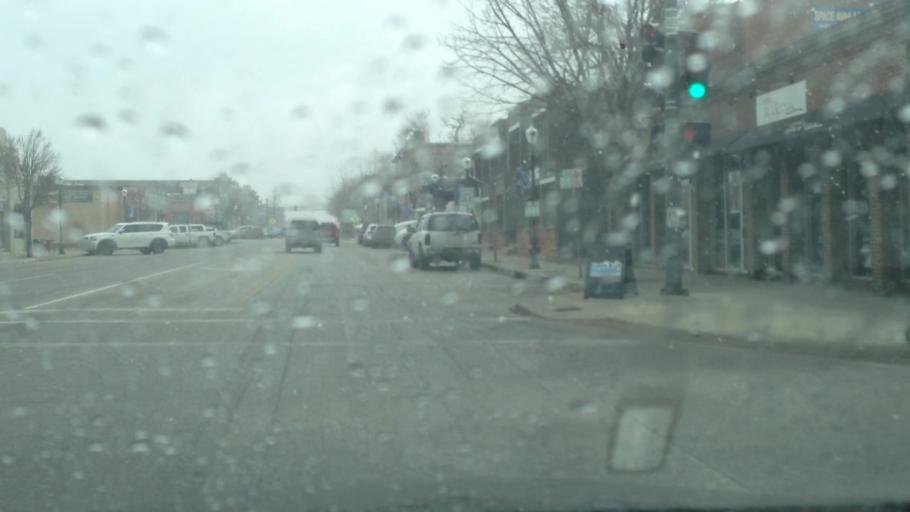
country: US
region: Colorado
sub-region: Douglas County
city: Castle Rock
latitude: 39.3744
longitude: -104.8600
